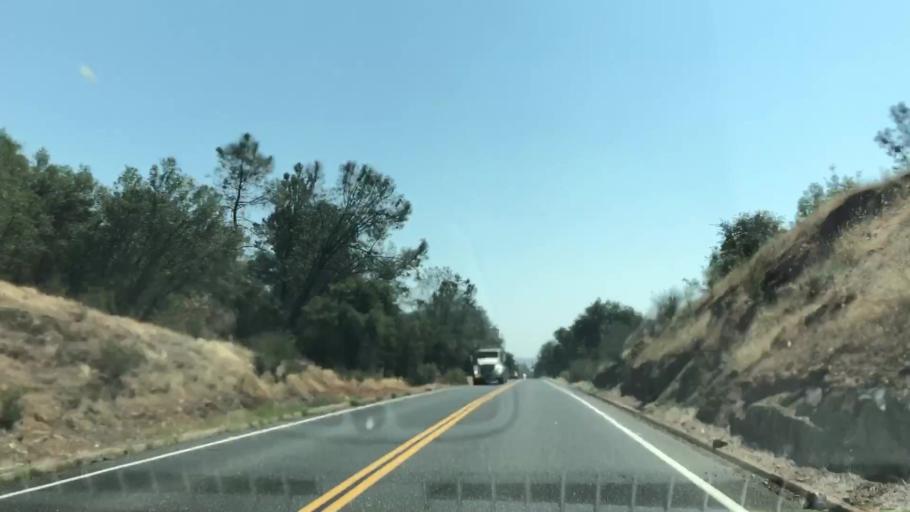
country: US
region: California
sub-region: Calaveras County
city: Copperopolis
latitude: 37.9468
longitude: -120.6094
